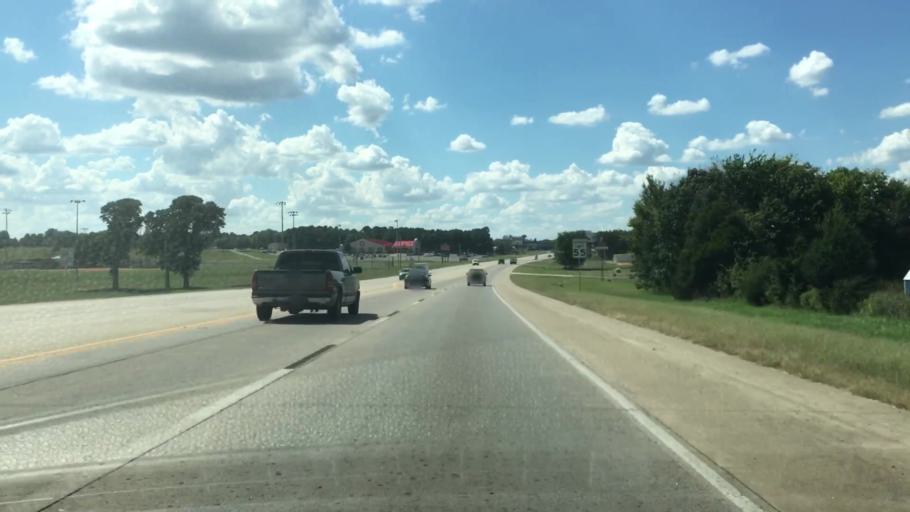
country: US
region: Oklahoma
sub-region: Cherokee County
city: Park Hill
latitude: 35.8498
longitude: -95.0043
